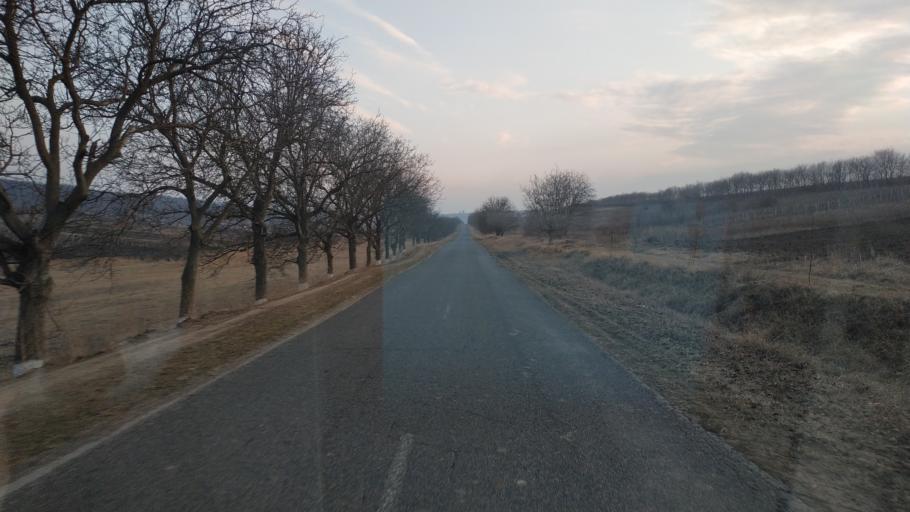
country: MD
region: Hincesti
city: Dancu
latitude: 46.6912
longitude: 28.3361
